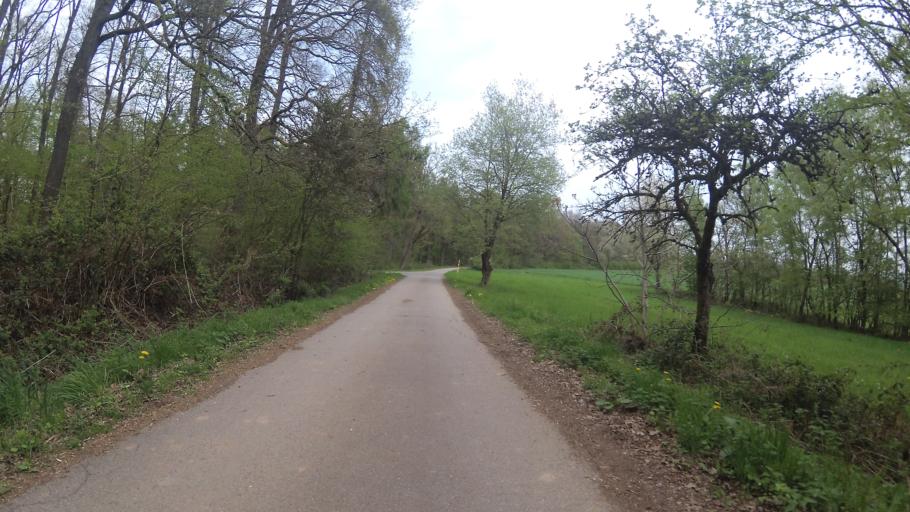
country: DE
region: Saarland
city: Mainzweiler
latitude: 49.4286
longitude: 7.1401
